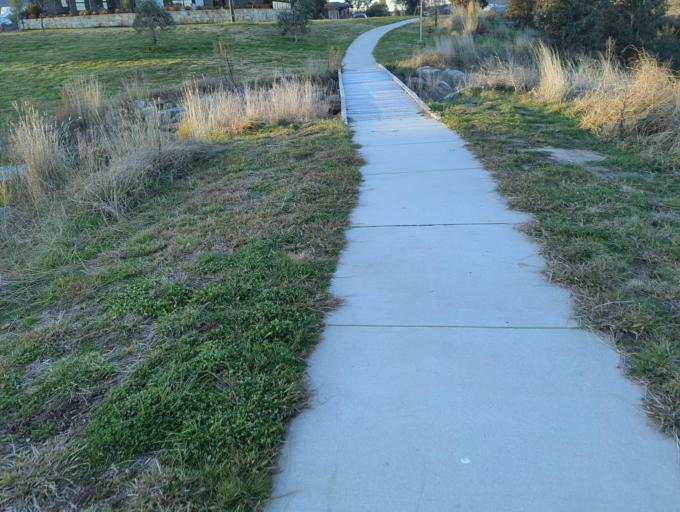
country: AU
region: New South Wales
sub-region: Queanbeyan
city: Queanbeyan
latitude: -35.4266
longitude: 149.2432
